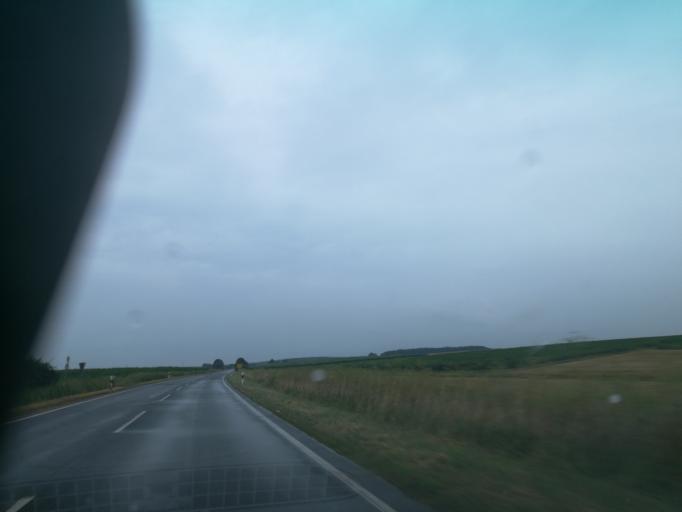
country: DE
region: Bavaria
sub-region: Regierungsbezirk Mittelfranken
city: Obermichelbach
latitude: 49.5324
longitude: 10.9537
